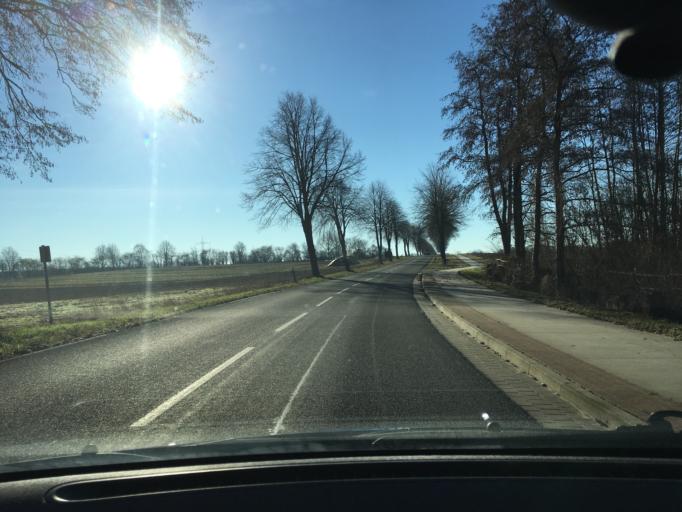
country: DE
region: Lower Saxony
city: Melbeck
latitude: 53.1695
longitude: 10.3817
